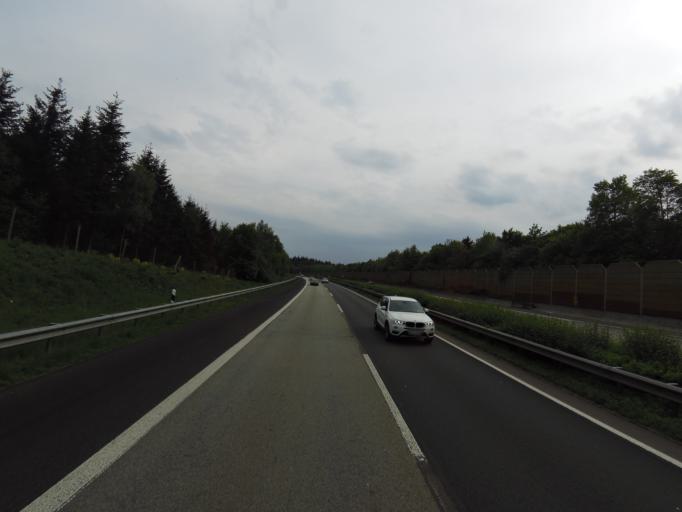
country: DE
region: Rheinland-Pfalz
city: Nortershausen
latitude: 50.2380
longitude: 7.5141
